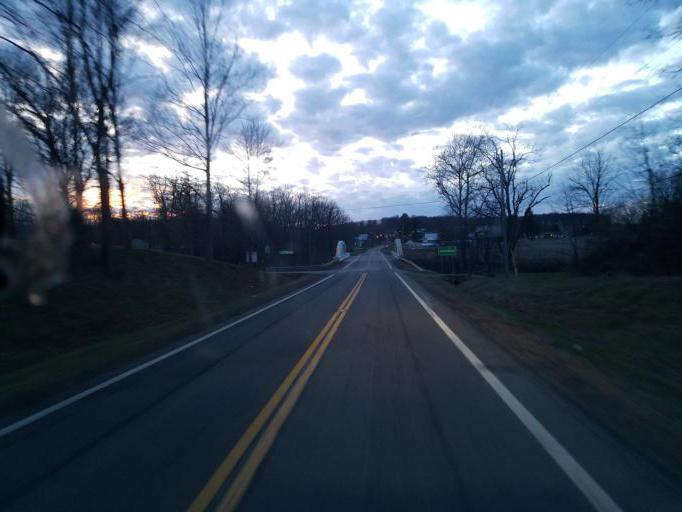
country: US
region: Ohio
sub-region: Knox County
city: Oak Hill
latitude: 40.2849
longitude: -82.2768
